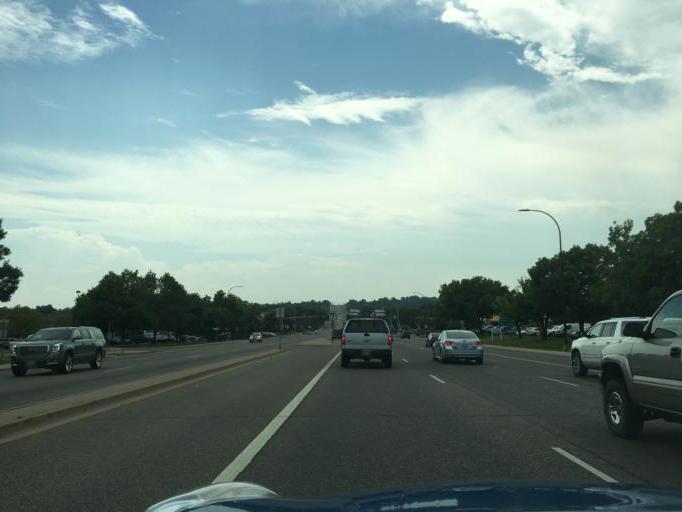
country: US
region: Colorado
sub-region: Jefferson County
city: Arvada
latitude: 39.8439
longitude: -105.0819
